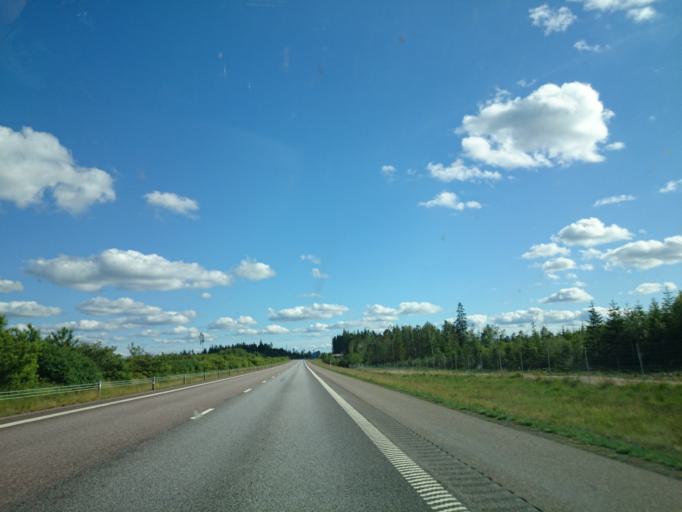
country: SE
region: Kronoberg
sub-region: Ljungby Kommun
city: Ljungby
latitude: 56.7149
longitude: 13.8397
